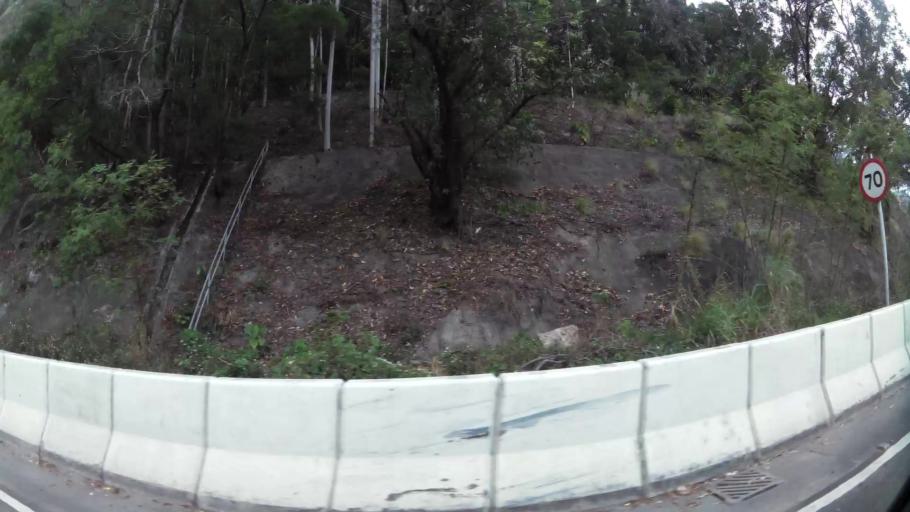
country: HK
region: Sham Shui Po
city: Sham Shui Po
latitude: 22.3405
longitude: 114.1446
